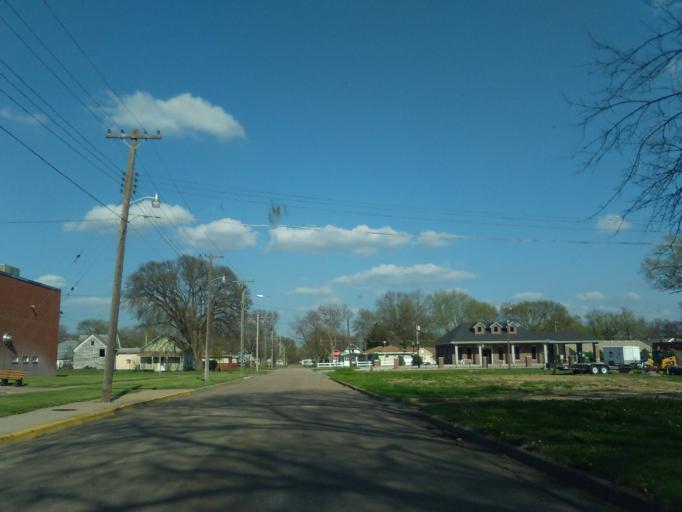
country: US
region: Nebraska
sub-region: Webster County
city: Red Cloud
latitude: 40.0919
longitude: -98.5203
